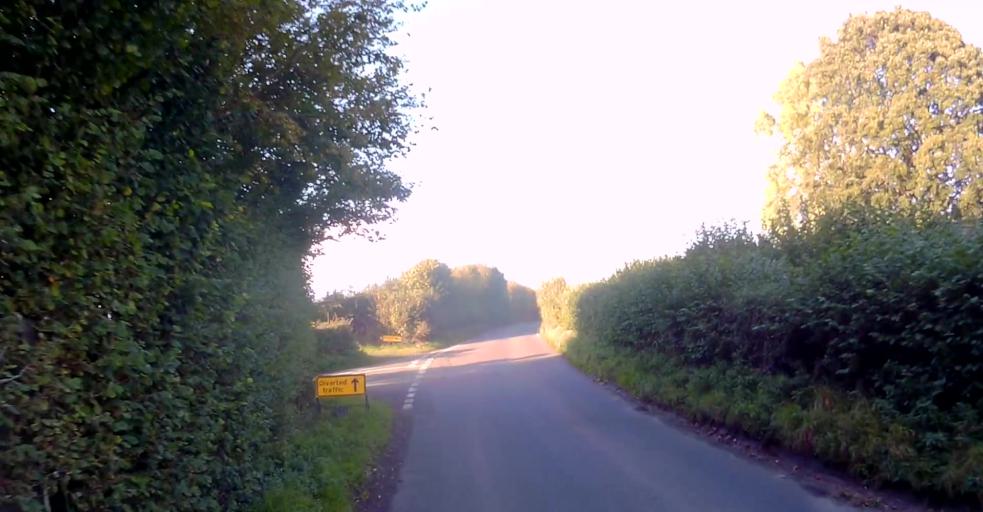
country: GB
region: England
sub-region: Hampshire
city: Long Sutton
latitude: 51.2318
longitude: -0.9268
